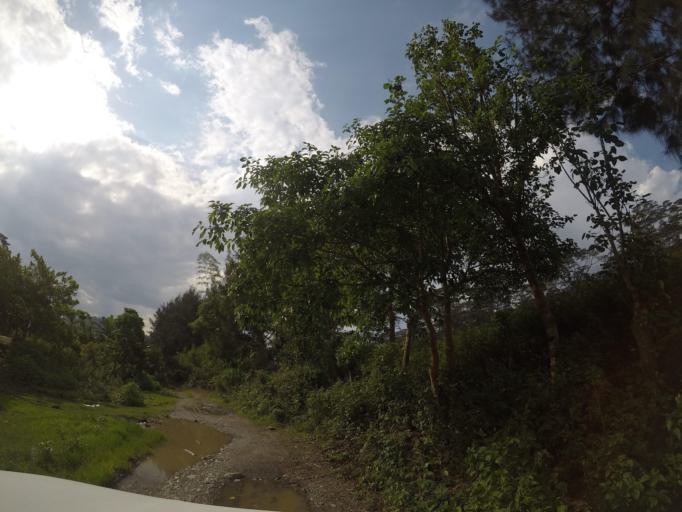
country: TL
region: Ermera
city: Gleno
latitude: -8.7119
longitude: 125.4396
